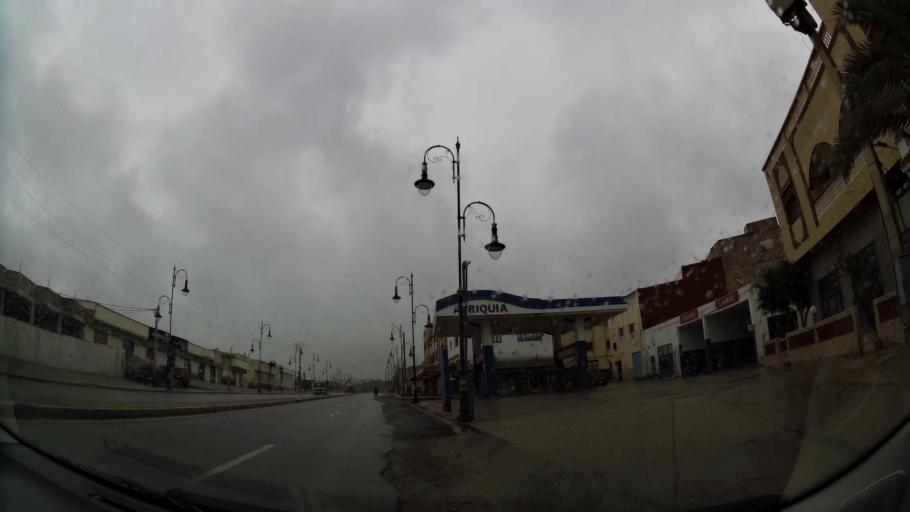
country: MA
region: Taza-Al Hoceima-Taounate
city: Imzourene
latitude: 35.1658
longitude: -3.8570
